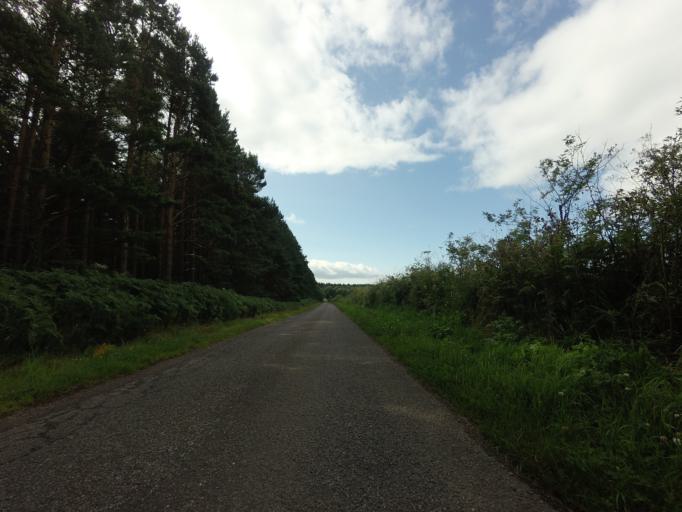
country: GB
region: Scotland
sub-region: Highland
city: Nairn
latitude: 57.5642
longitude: -3.8669
